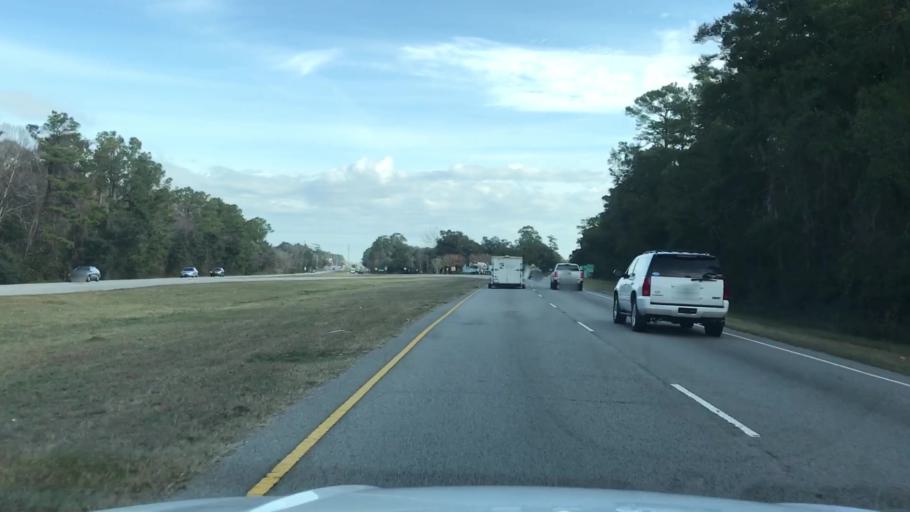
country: US
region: South Carolina
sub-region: Georgetown County
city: Murrells Inlet
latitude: 33.5268
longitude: -79.0638
